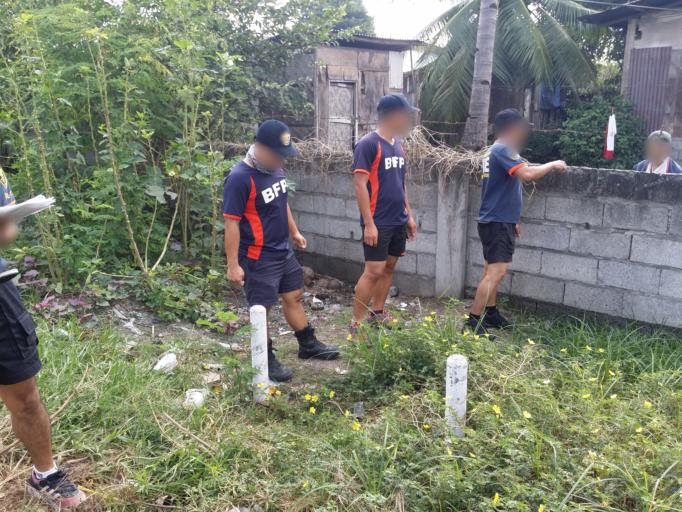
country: PH
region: Soccsksargen
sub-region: General Santos City
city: General Santos
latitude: 6.1282
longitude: 125.1299
